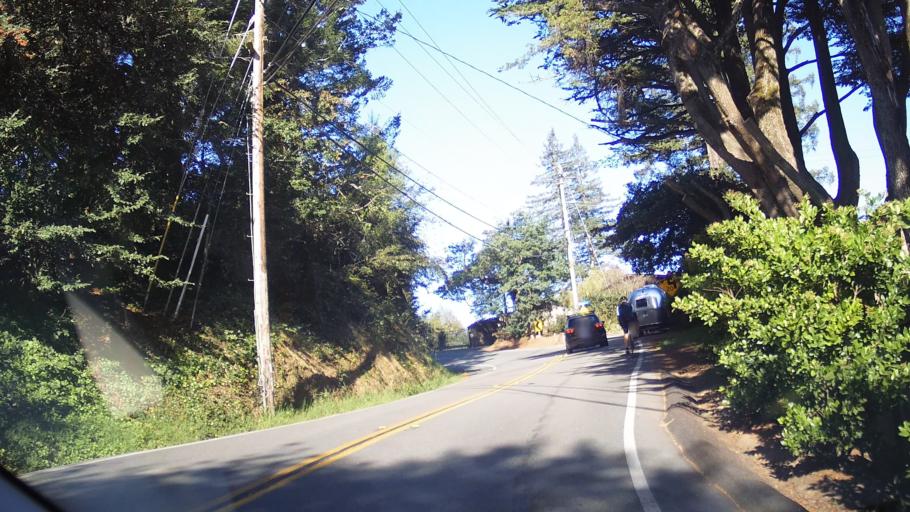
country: US
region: California
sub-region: Marin County
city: Mill Valley
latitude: 37.9002
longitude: -122.5639
